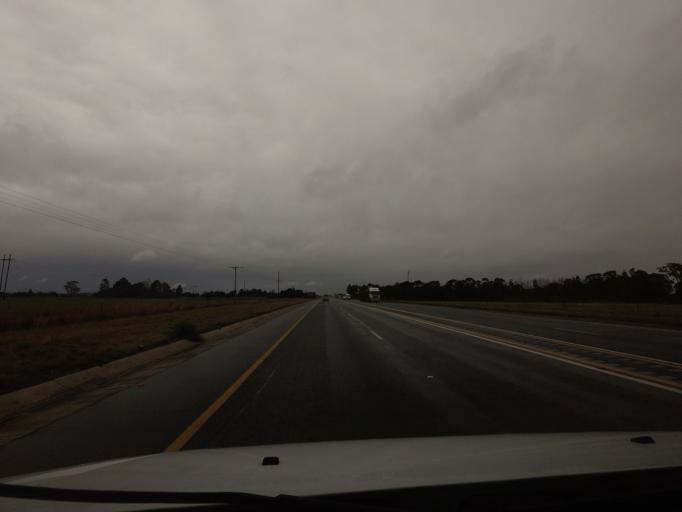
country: ZA
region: Mpumalanga
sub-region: Nkangala District Municipality
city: Belfast
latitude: -25.7208
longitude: 30.0448
